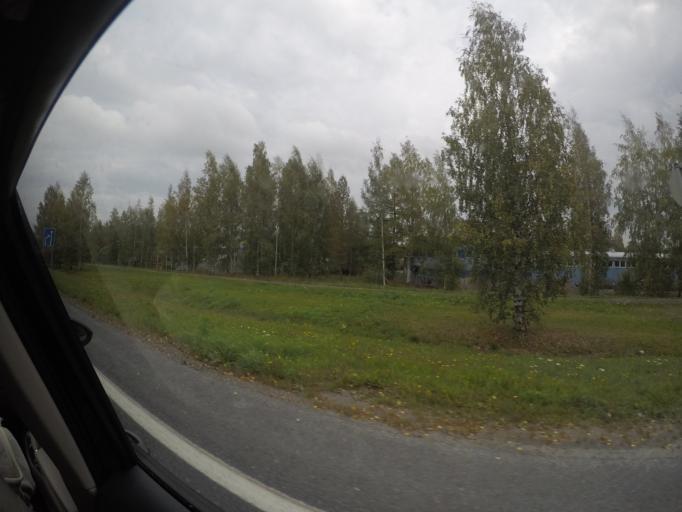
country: FI
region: Haeme
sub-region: Haemeenlinna
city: Haemeenlinna
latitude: 61.0158
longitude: 24.4199
